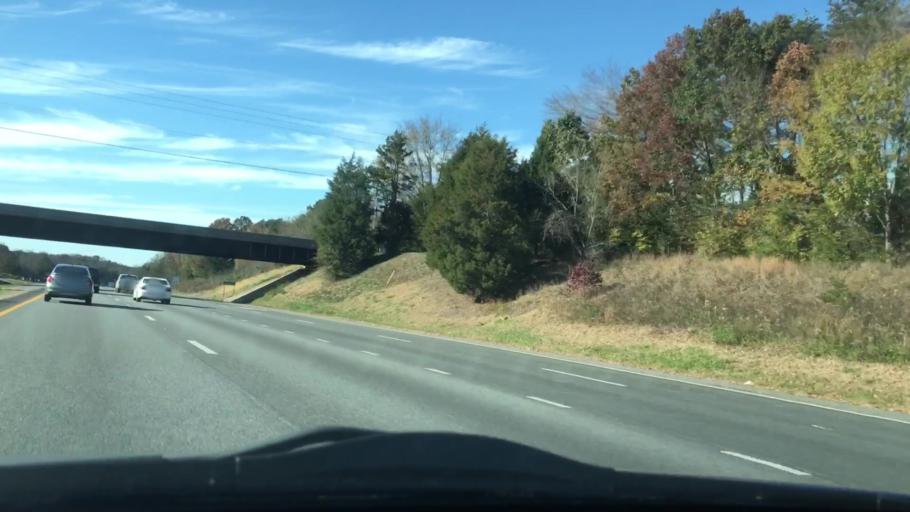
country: US
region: North Carolina
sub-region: Guilford County
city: High Point
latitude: 36.0171
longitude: -80.0419
